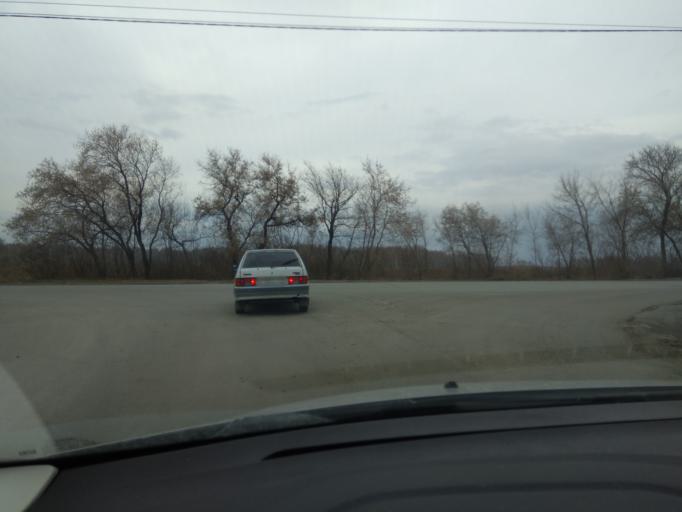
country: RU
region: Chelyabinsk
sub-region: Gorod Chelyabinsk
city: Chelyabinsk
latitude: 55.2865
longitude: 61.5104
